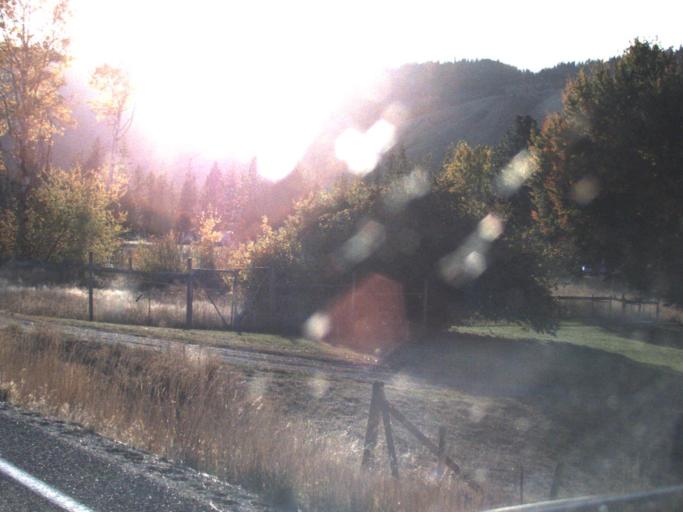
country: US
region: Washington
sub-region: Stevens County
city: Kettle Falls
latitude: 48.7529
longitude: -118.0437
